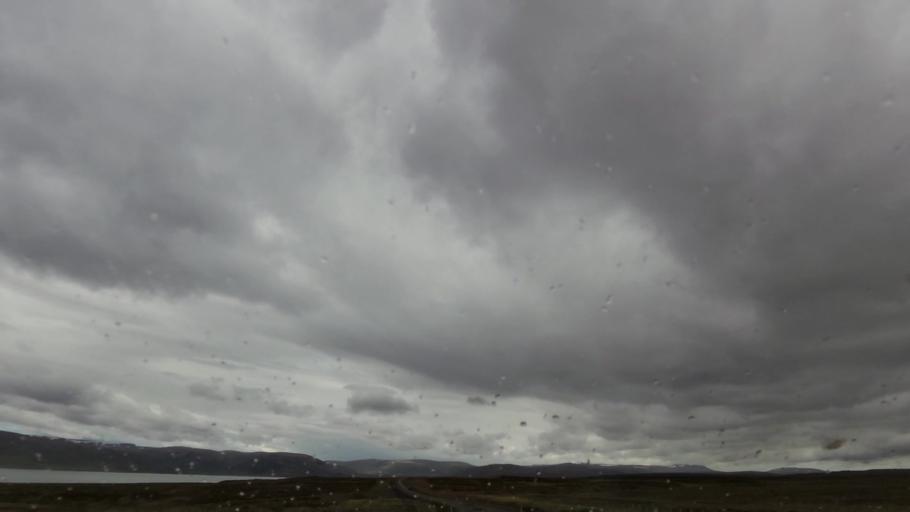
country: IS
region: West
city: Borgarnes
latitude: 65.1365
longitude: -21.7262
